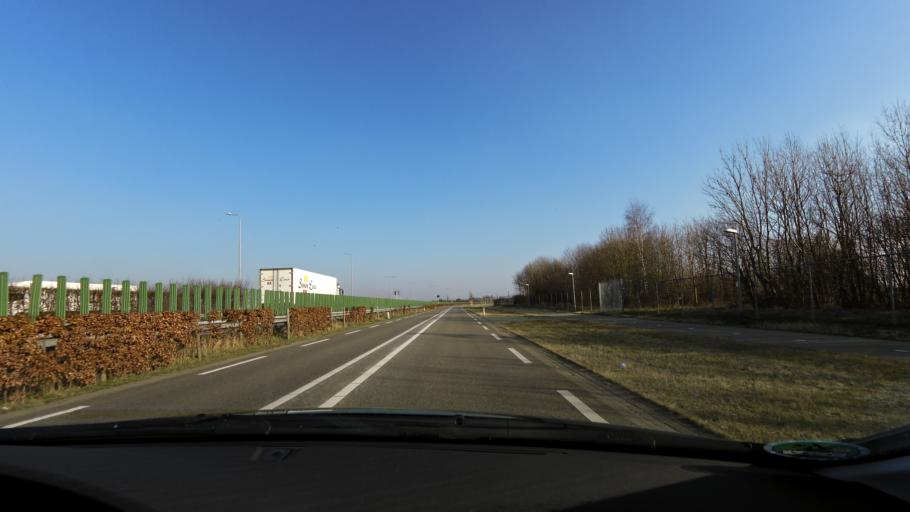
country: NL
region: Limburg
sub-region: Gemeente Meerssen
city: Meerssen
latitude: 50.9040
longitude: 5.7583
